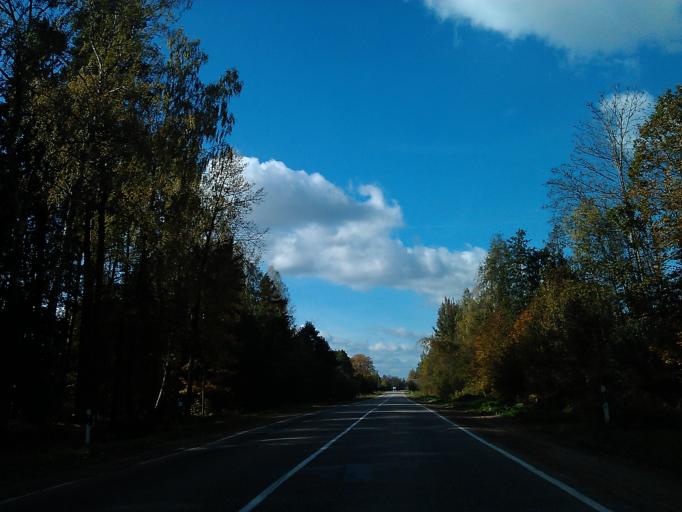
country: LV
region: Livani
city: Livani
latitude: 56.2175
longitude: 26.2431
